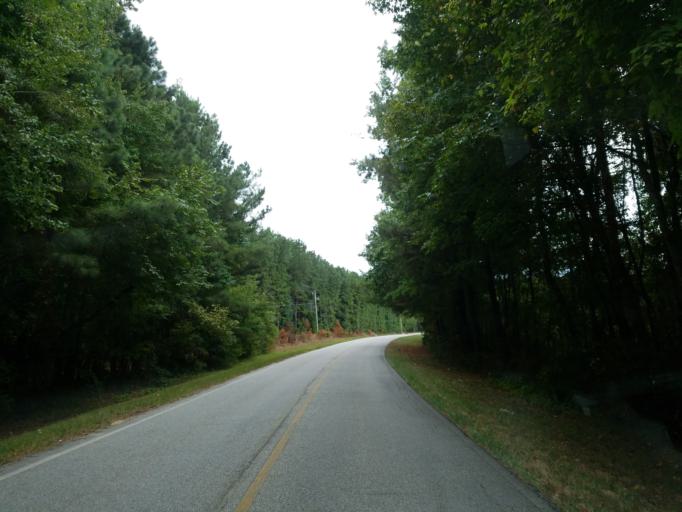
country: US
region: Georgia
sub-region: Clayton County
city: Lovejoy
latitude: 33.4197
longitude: -84.3117
